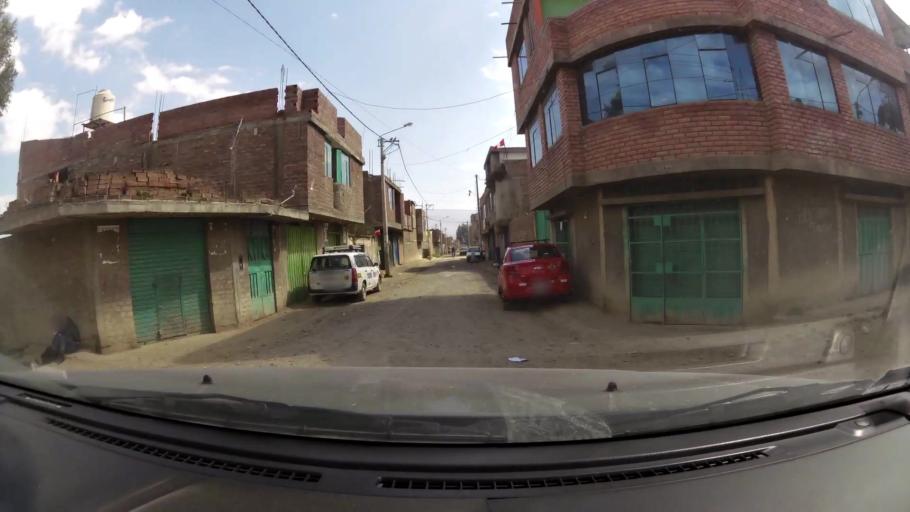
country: PE
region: Junin
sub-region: Provincia de Huancayo
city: Huancayo
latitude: -12.0951
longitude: -75.1996
